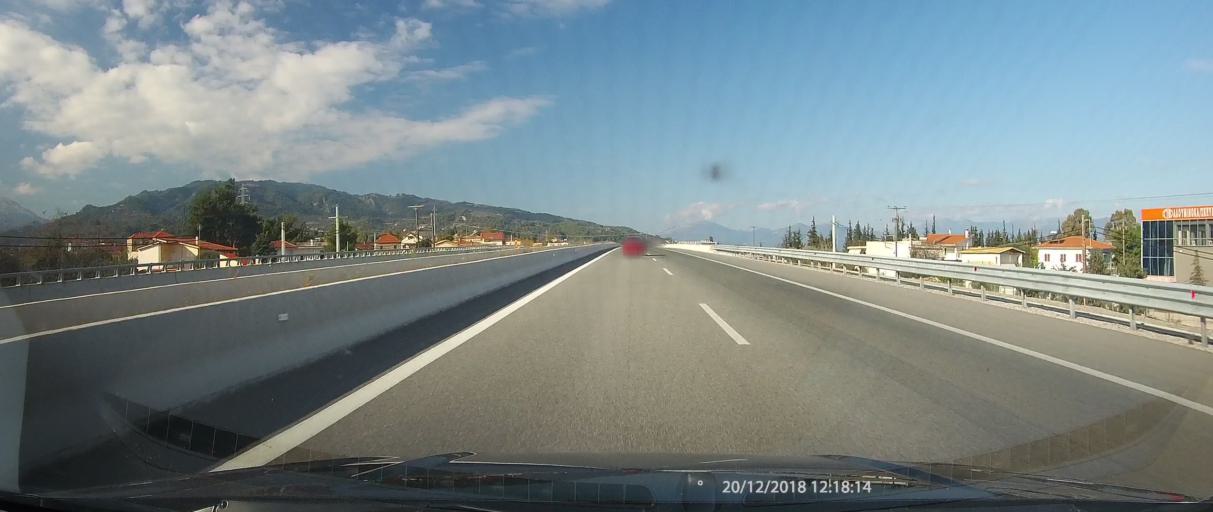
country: GR
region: West Greece
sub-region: Nomos Achaias
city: Kamarai
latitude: 38.2950
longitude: 22.0074
